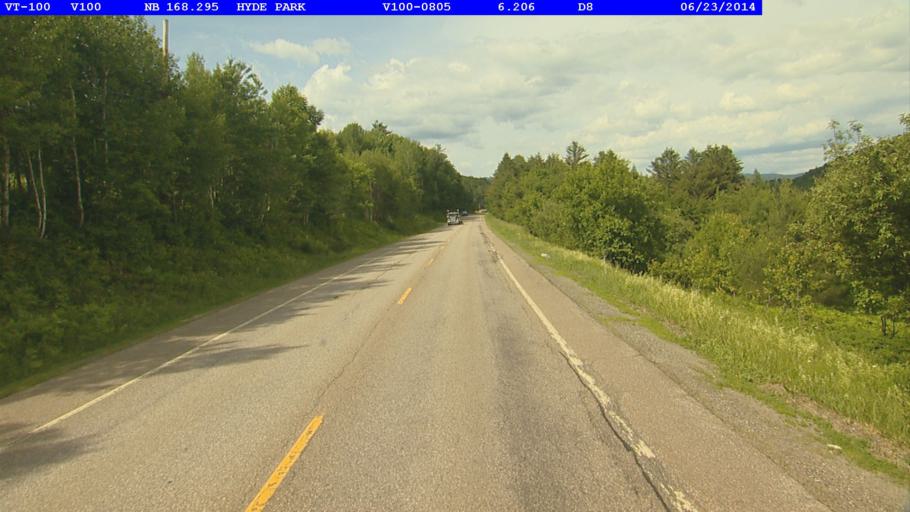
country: US
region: Vermont
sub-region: Lamoille County
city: Hyde Park
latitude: 44.6797
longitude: -72.5931
